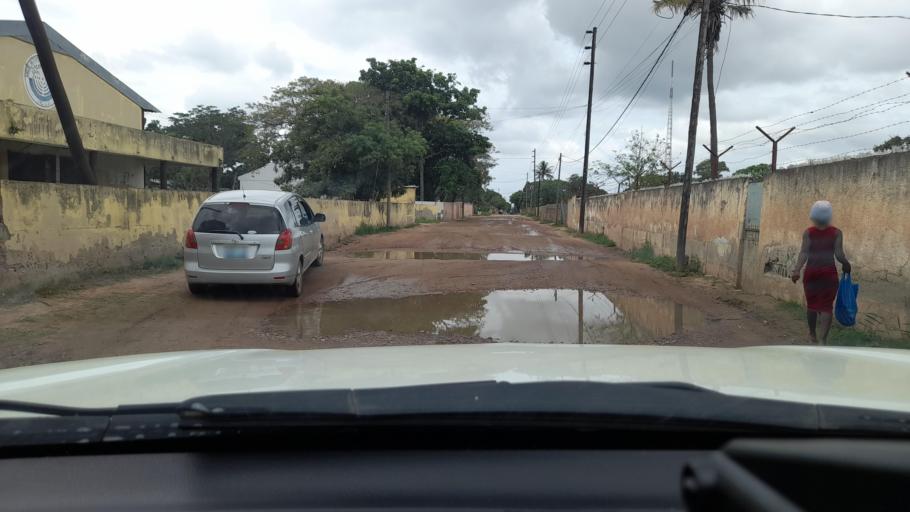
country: MZ
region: Maputo
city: Matola
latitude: -25.9028
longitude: 32.4878
